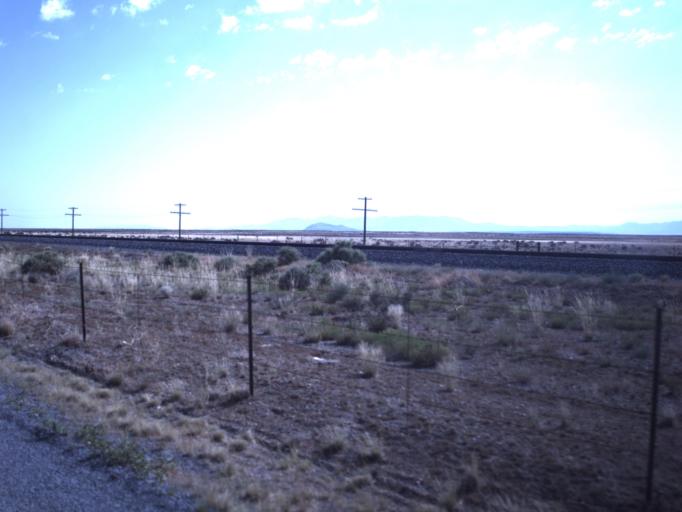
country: US
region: Utah
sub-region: Millard County
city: Delta
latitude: 38.9262
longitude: -112.8107
